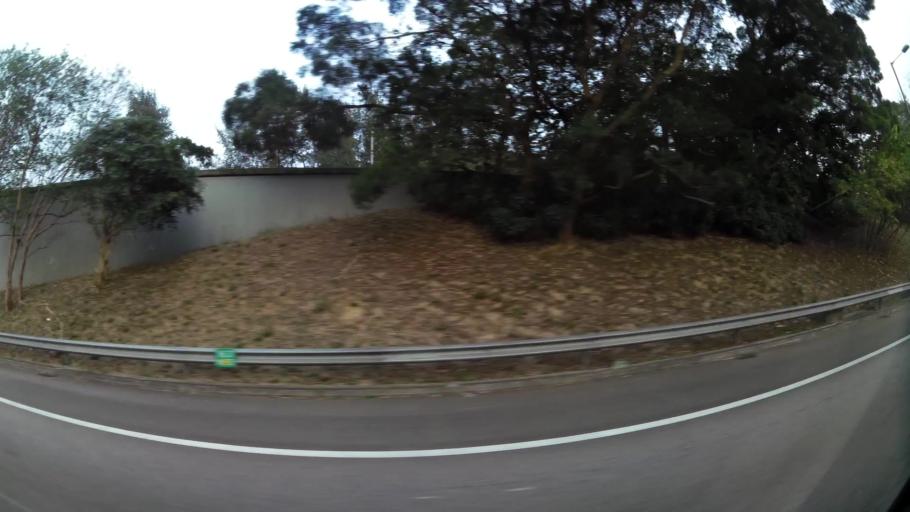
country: HK
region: Sha Tin
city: Sha Tin
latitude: 22.3966
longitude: 114.2106
